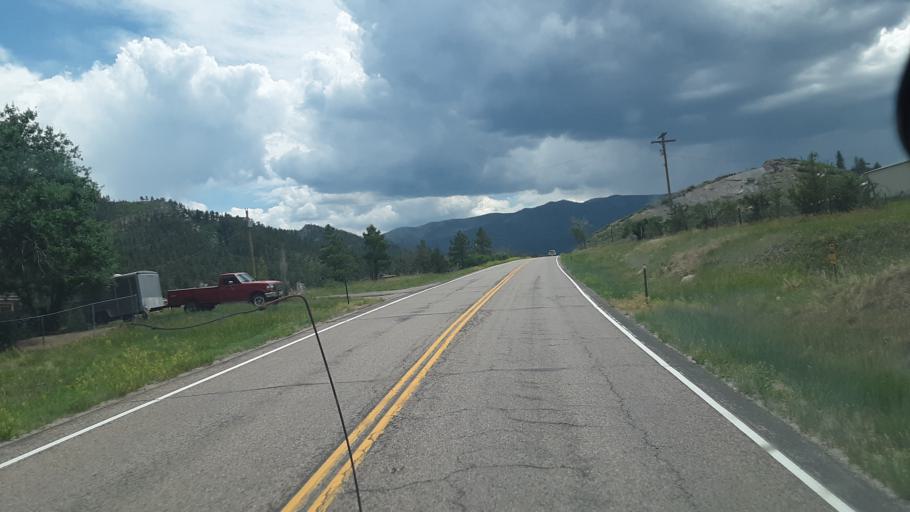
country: US
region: Colorado
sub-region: Fremont County
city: Florence
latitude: 38.2138
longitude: -105.0940
